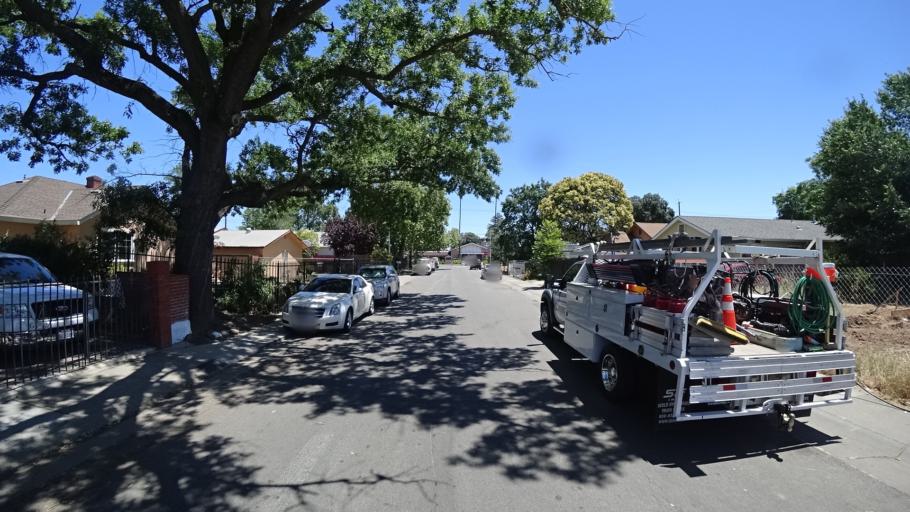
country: US
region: California
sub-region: Sacramento County
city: Parkway
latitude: 38.5345
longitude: -121.4657
